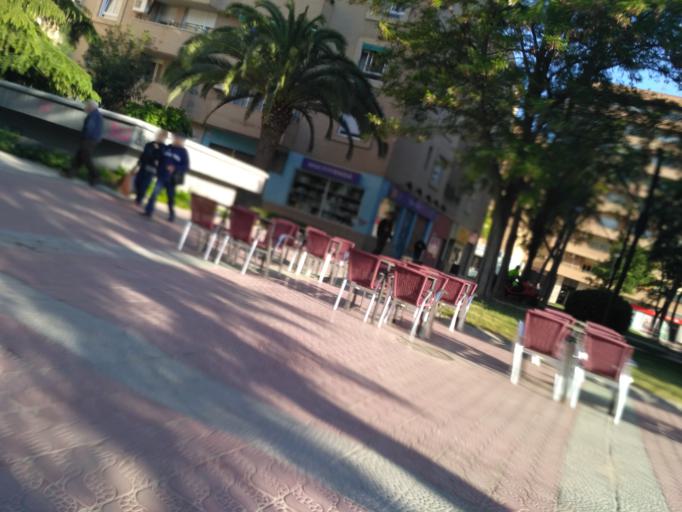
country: ES
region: Aragon
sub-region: Provincia de Zaragoza
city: Almozara
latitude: 41.6652
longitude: -0.8891
